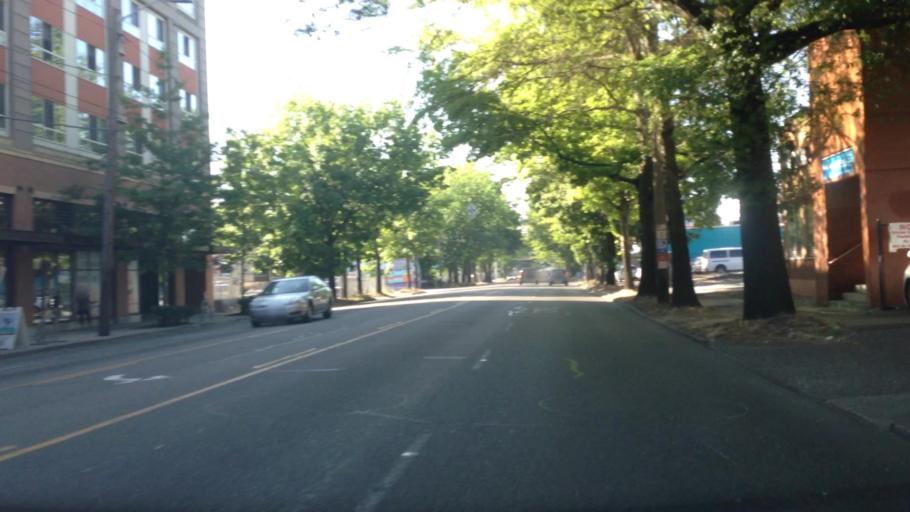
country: US
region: Washington
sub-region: King County
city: Seattle
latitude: 47.5731
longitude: -122.2941
